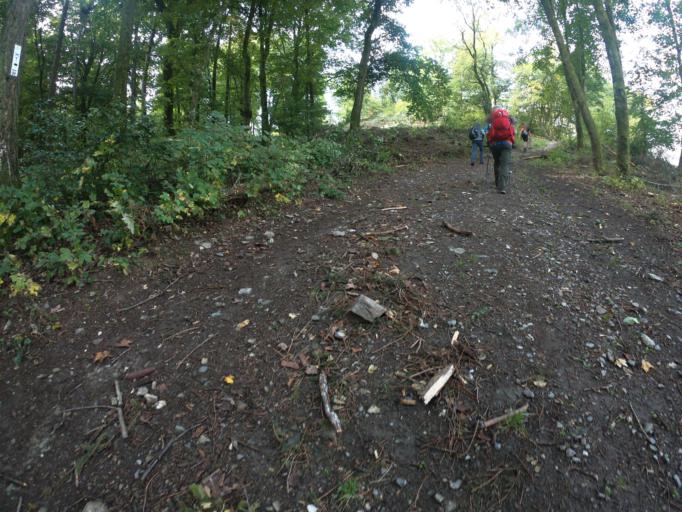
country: DE
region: Hesse
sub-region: Regierungsbezirk Darmstadt
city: Niedernhausen
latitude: 50.1386
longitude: 8.2844
